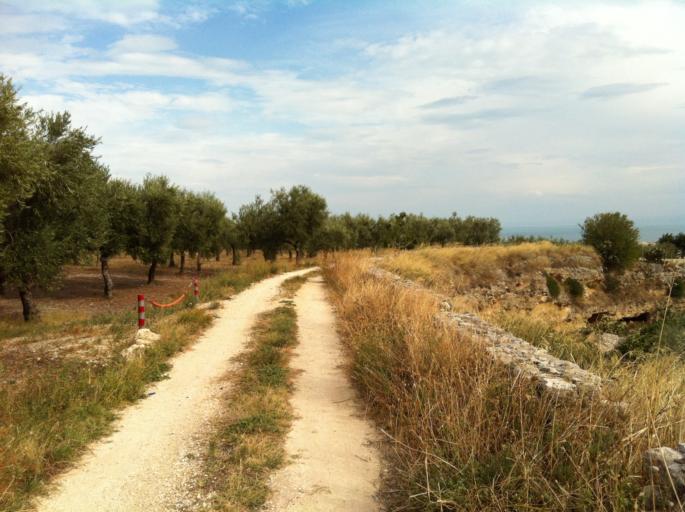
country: IT
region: Apulia
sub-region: Provincia di Foggia
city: Manfredonia
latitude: 41.6625
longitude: 15.9133
